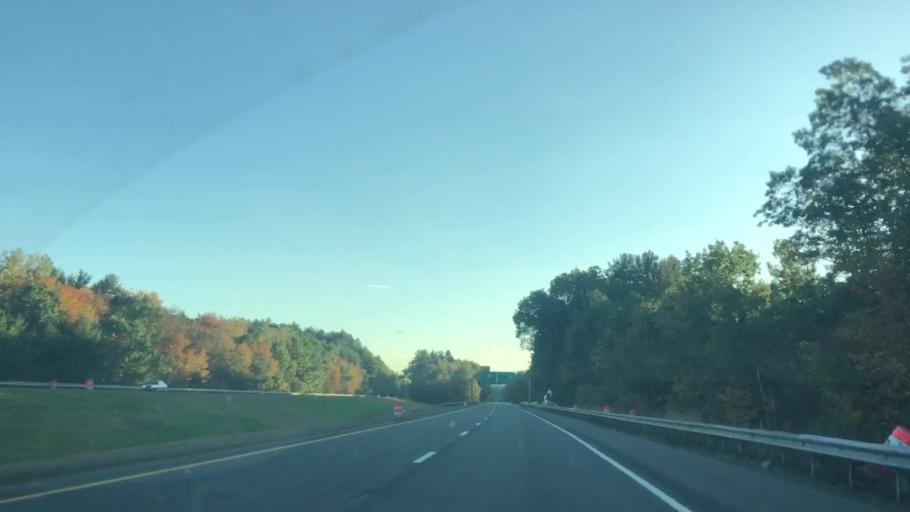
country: US
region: Massachusetts
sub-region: Franklin County
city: Turners Falls
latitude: 42.6334
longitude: -72.5793
